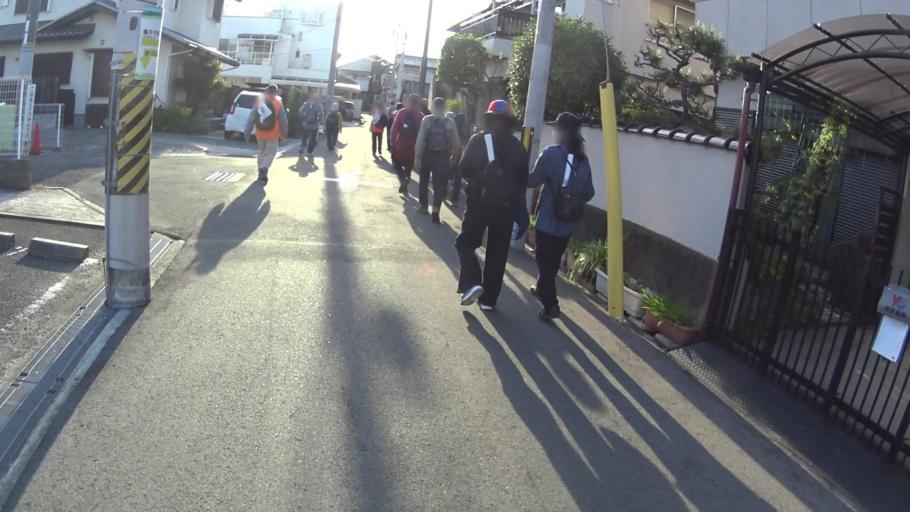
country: JP
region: Osaka
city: Kashihara
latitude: 34.5801
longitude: 135.5939
